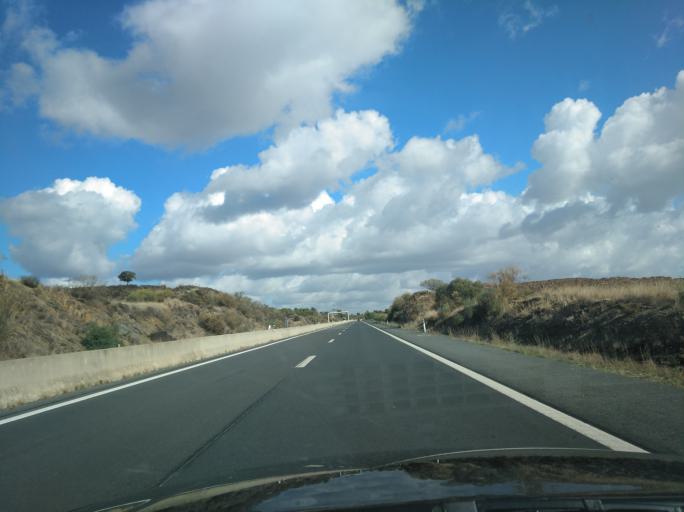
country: PT
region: Faro
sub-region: Vila Real de Santo Antonio
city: Monte Gordo
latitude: 37.2032
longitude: -7.4919
